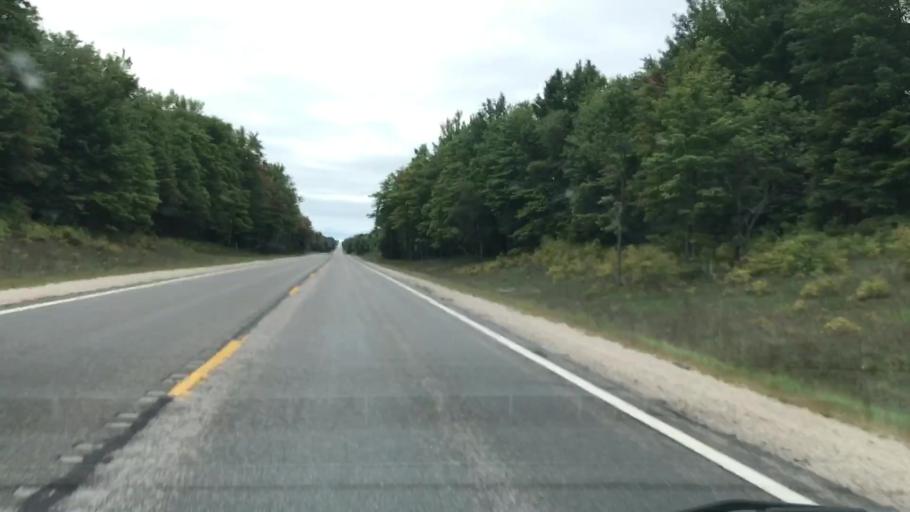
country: US
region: Michigan
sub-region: Luce County
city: Newberry
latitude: 46.2424
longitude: -85.5723
